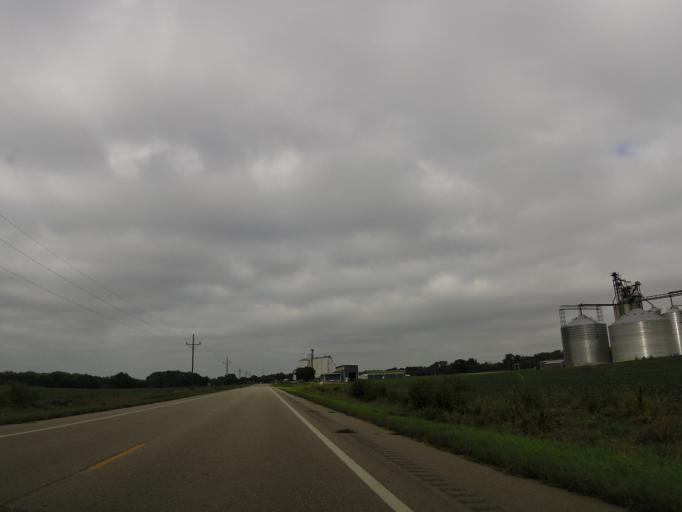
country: US
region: Minnesota
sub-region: Chippewa County
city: Montevideo
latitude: 44.9114
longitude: -95.6913
